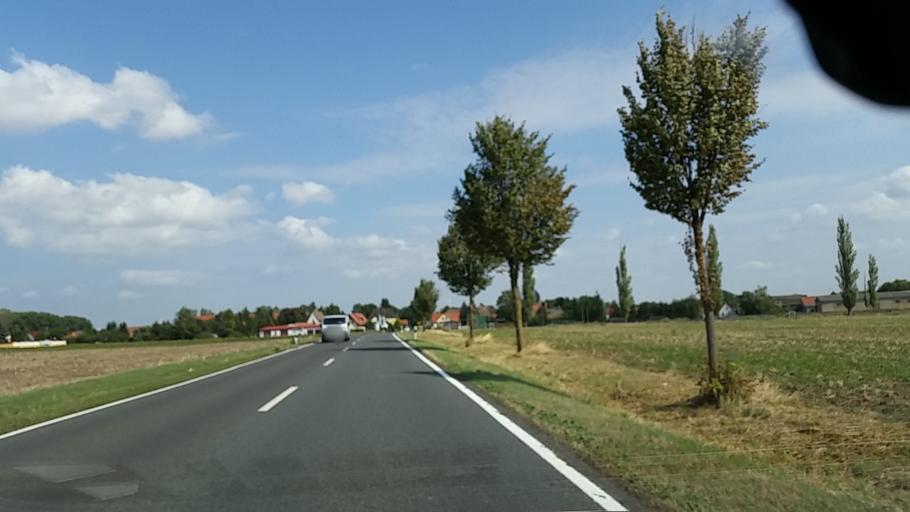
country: DE
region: Thuringia
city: Ringleben
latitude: 51.3640
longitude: 11.2126
